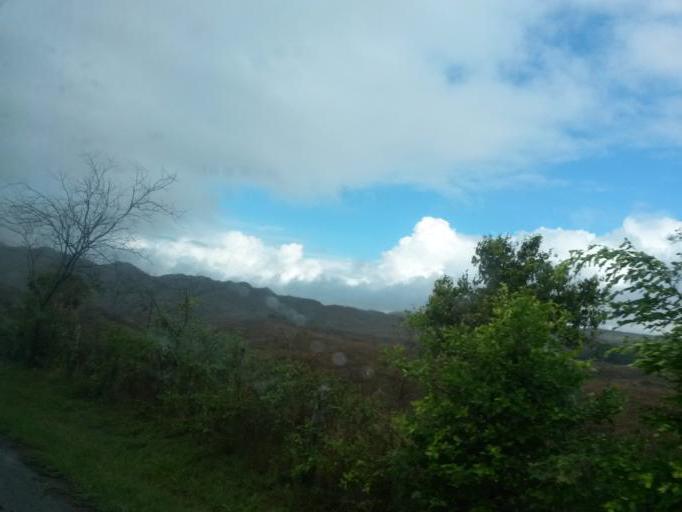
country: CO
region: Cauca
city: El Bordo
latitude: 2.1469
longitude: -76.9271
